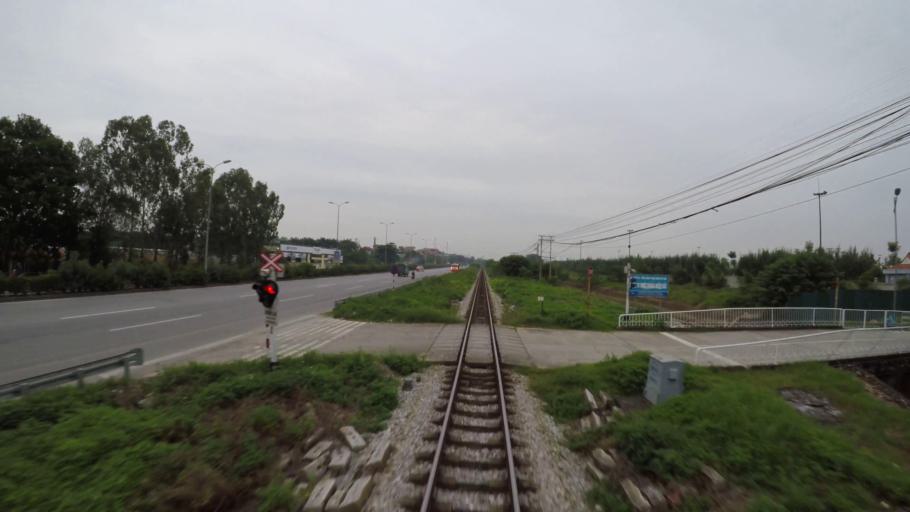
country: VN
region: Ha Noi
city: Trau Quy
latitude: 21.0138
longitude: 105.9483
